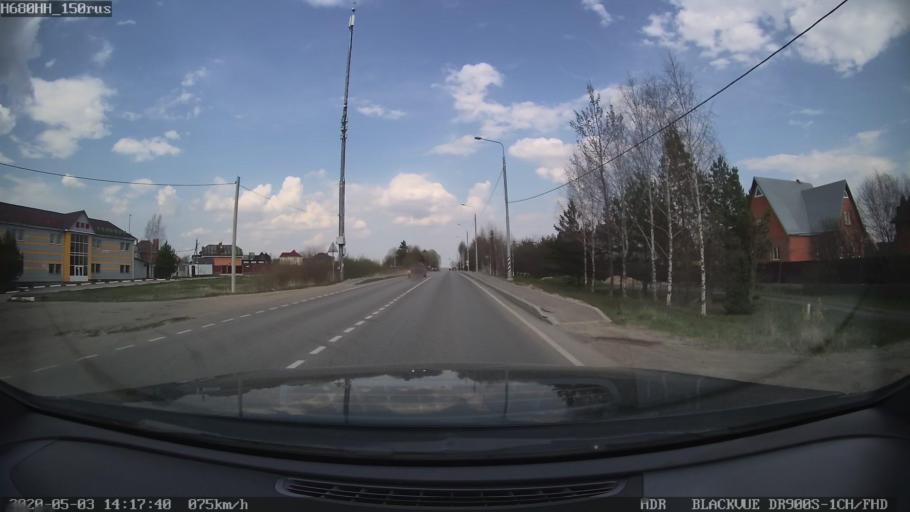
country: RU
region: Moskovskaya
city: Solnechnogorsk
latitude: 56.2108
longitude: 36.9671
